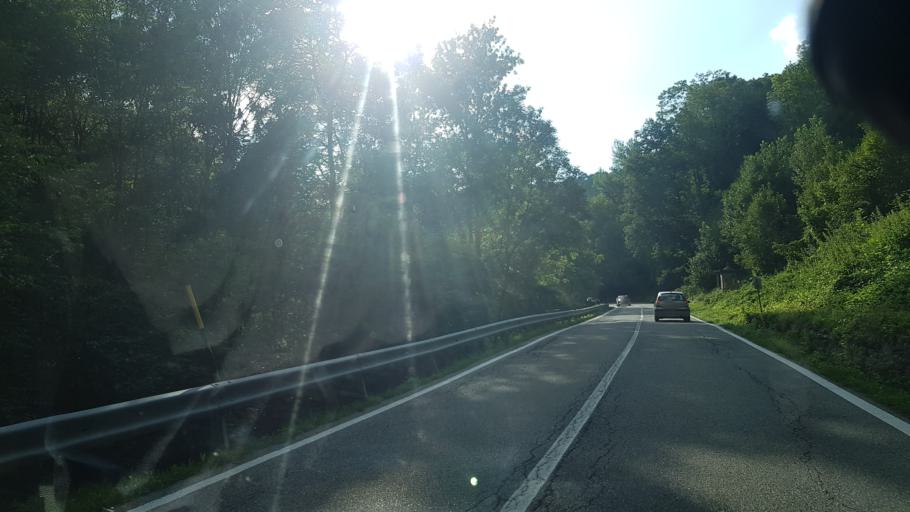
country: IT
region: Piedmont
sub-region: Provincia di Cuneo
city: Frassino
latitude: 44.5714
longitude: 7.2707
